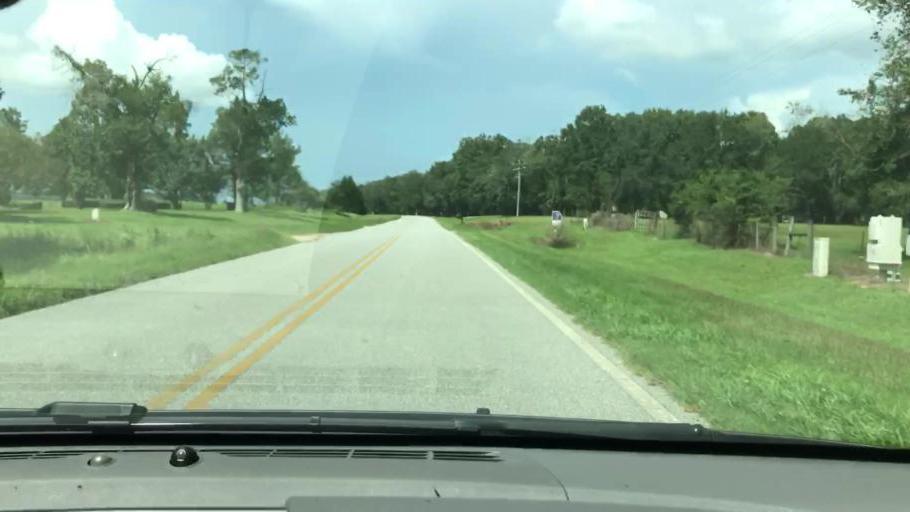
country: US
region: Georgia
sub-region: Seminole County
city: Donalsonville
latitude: 31.0825
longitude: -84.9962
